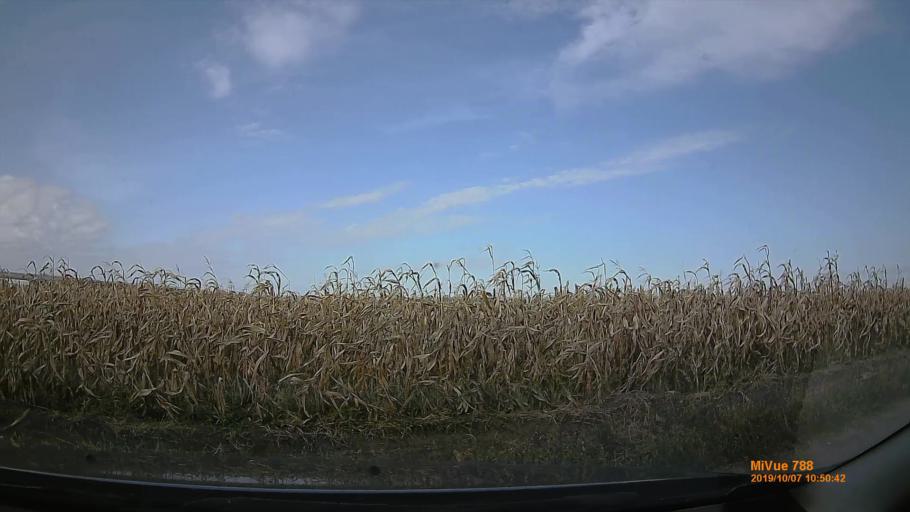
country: HU
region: Bekes
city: Kondoros
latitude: 46.7378
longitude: 20.8118
